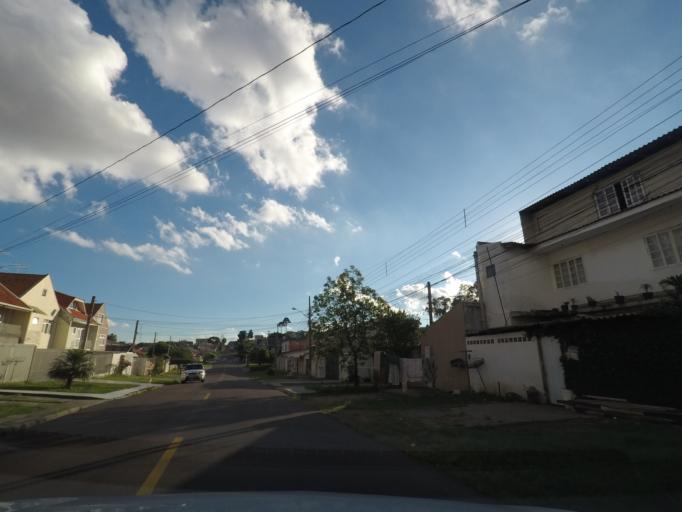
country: BR
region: Parana
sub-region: Sao Jose Dos Pinhais
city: Sao Jose dos Pinhais
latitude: -25.4949
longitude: -49.2547
